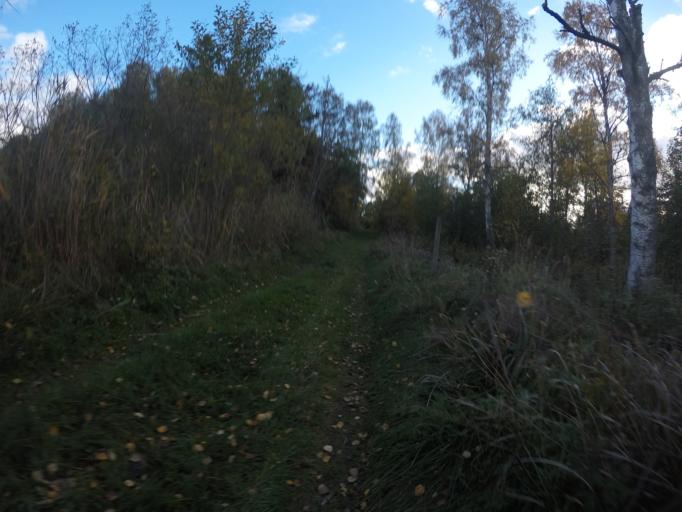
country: SE
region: Vaestmanland
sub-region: Arboga Kommun
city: Tyringe
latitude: 59.3223
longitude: 15.9737
